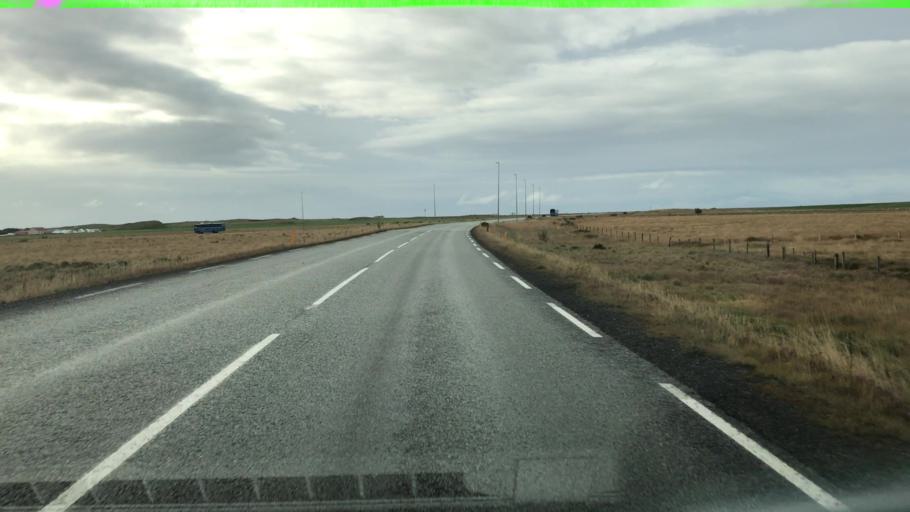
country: IS
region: West
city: Akranes
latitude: 64.3093
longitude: -21.9847
